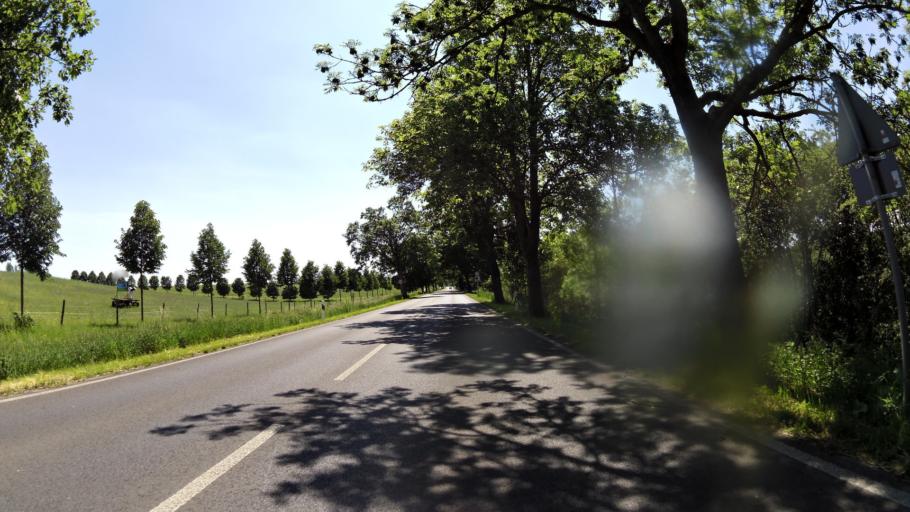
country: DE
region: Brandenburg
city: Lebus
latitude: 52.4166
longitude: 14.5283
